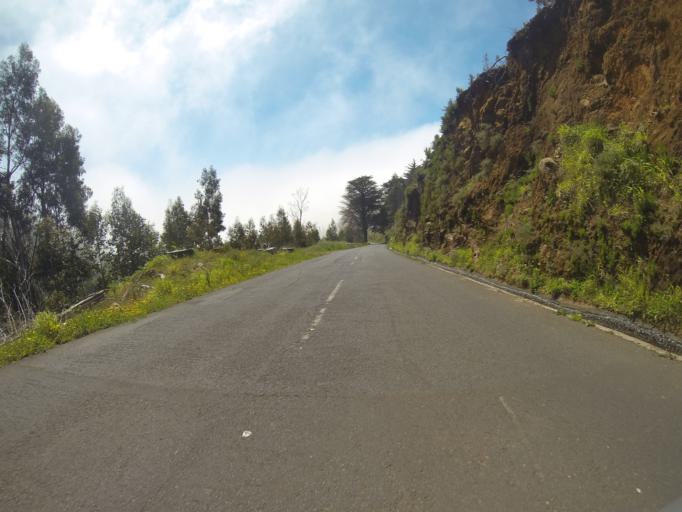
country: PT
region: Madeira
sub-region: Funchal
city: Nossa Senhora do Monte
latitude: 32.6926
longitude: -16.9001
